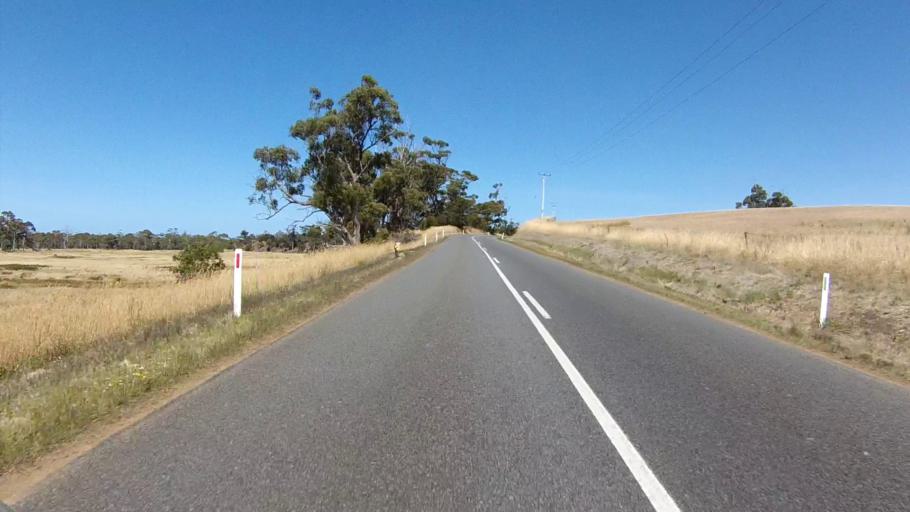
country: AU
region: Tasmania
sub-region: Sorell
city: Sorell
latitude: -42.2659
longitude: 148.0028
